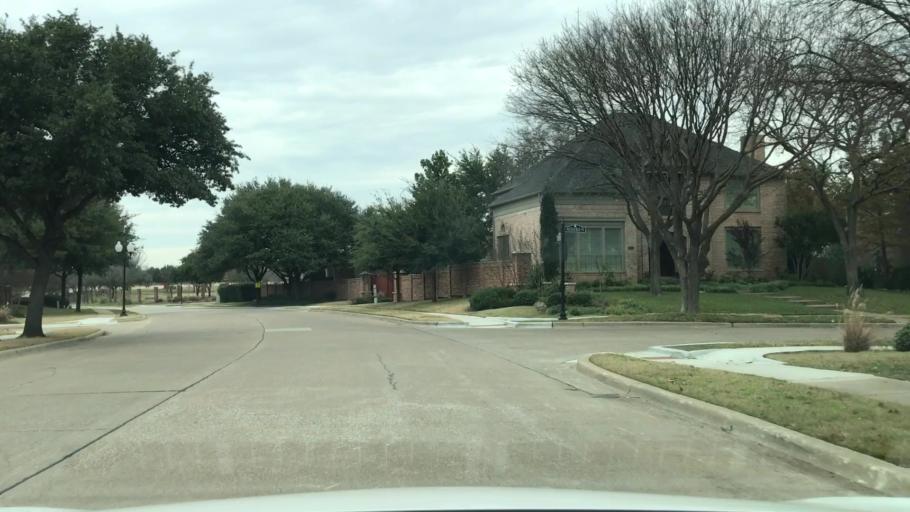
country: US
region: Texas
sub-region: Dallas County
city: Coppell
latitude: 32.9137
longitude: -96.9784
